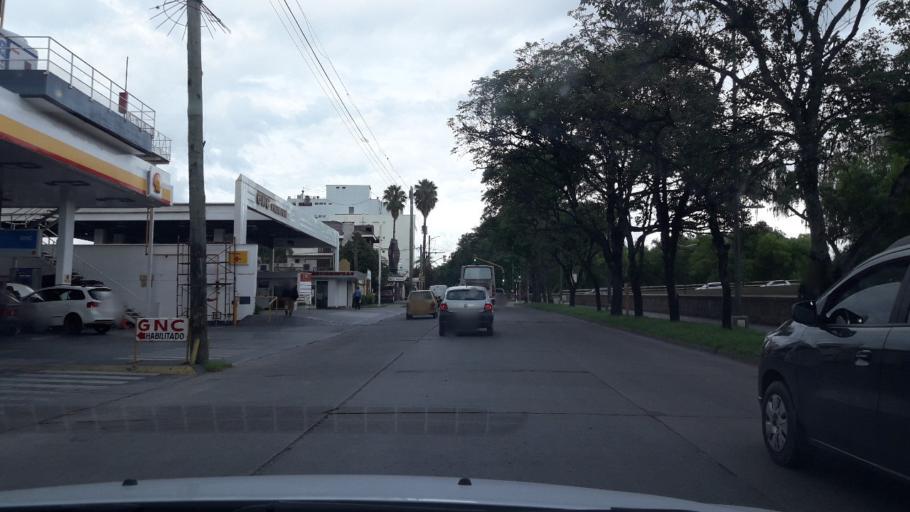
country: AR
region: Jujuy
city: San Salvador de Jujuy
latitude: -24.1904
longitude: -65.2954
